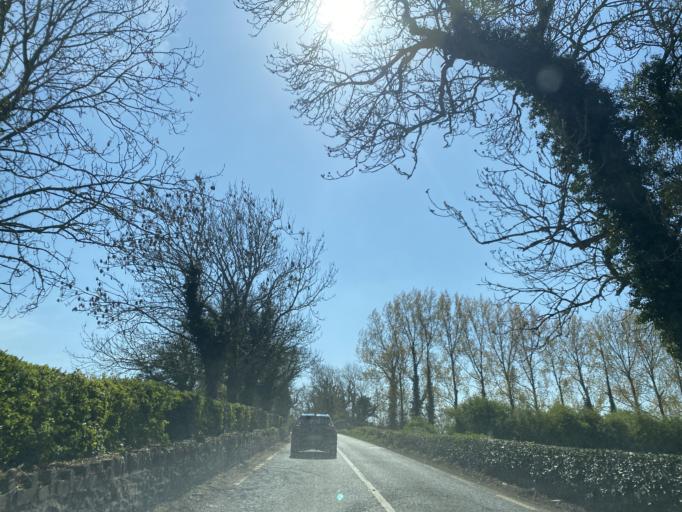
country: IE
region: Leinster
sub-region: Kildare
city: Kill
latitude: 53.2859
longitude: -6.6020
